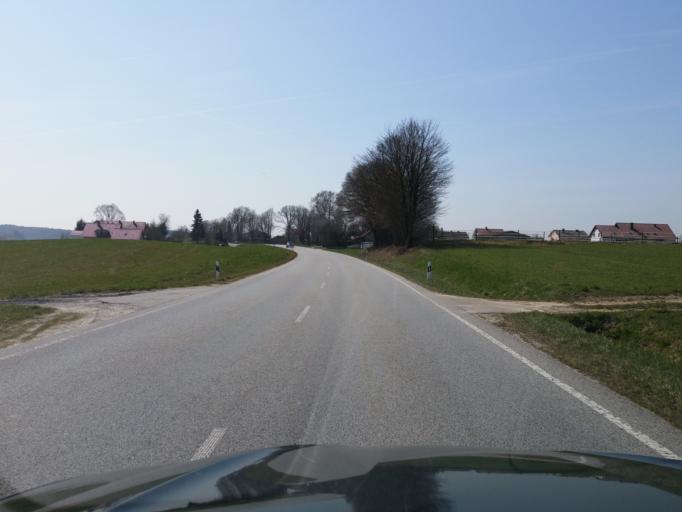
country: DE
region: Bavaria
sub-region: Lower Bavaria
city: Altfraunhofen
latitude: 48.4599
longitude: 12.1499
